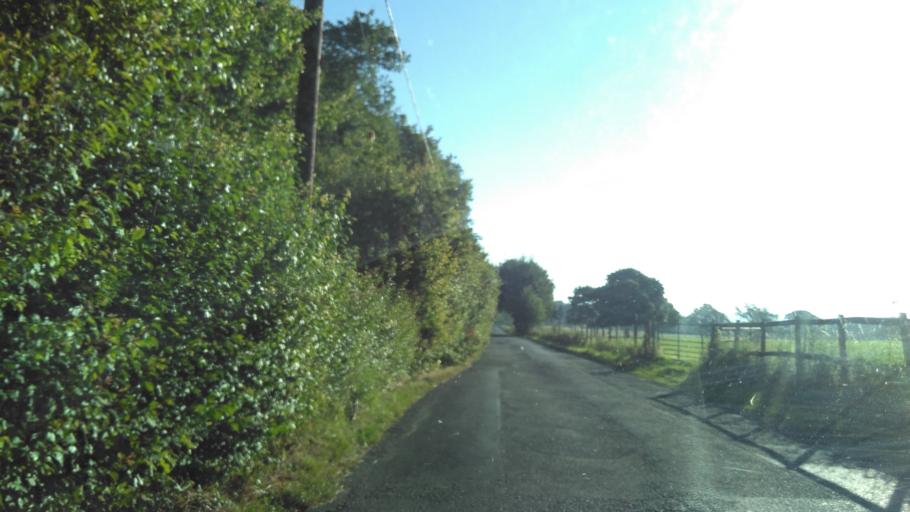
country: GB
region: England
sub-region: Kent
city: Dunkirk
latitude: 51.3052
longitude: 0.9891
